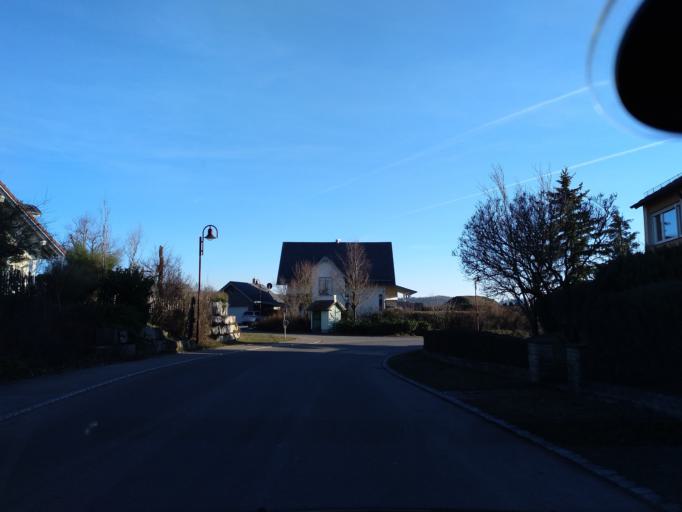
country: DE
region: Baden-Wuerttemberg
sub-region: Regierungsbezirk Stuttgart
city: Obersontheim
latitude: 49.0983
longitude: 9.9559
